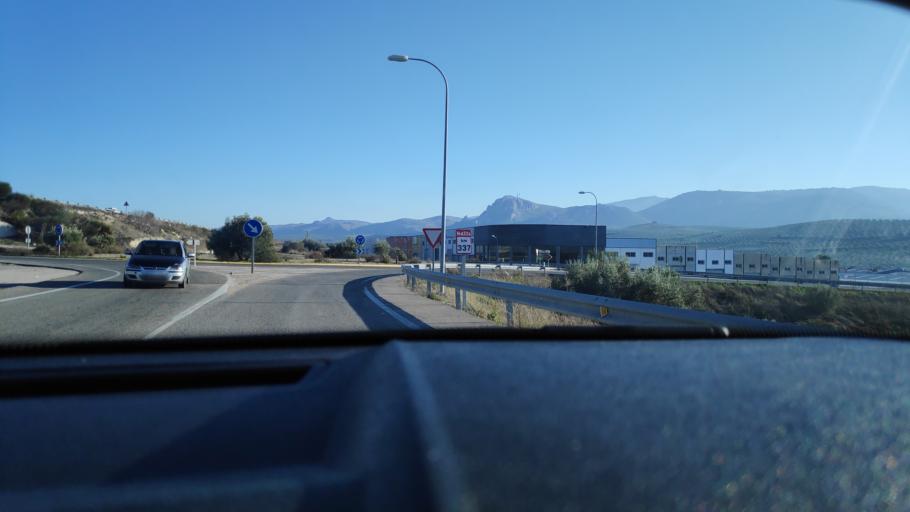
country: ES
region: Andalusia
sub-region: Province of Cordoba
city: Baena
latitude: 37.5958
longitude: -4.3034
